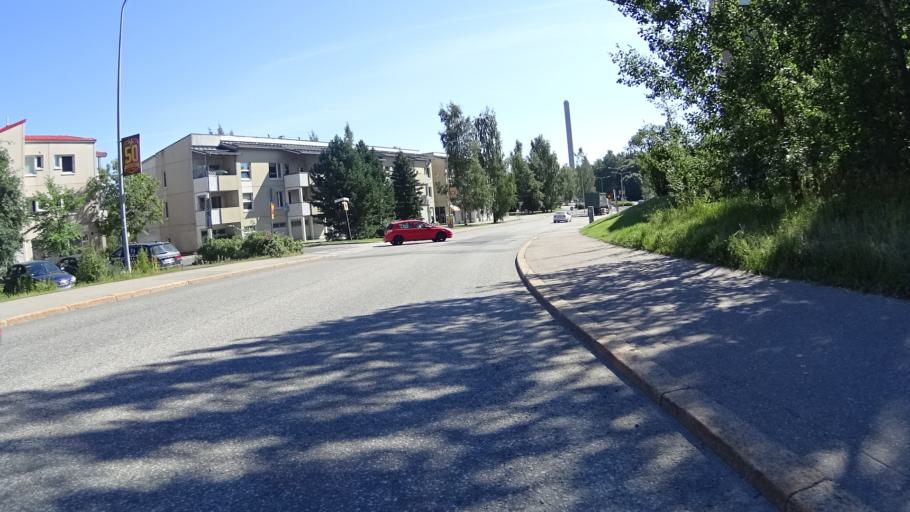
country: FI
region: Uusimaa
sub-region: Helsinki
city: Teekkarikylae
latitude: 60.2395
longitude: 24.8878
